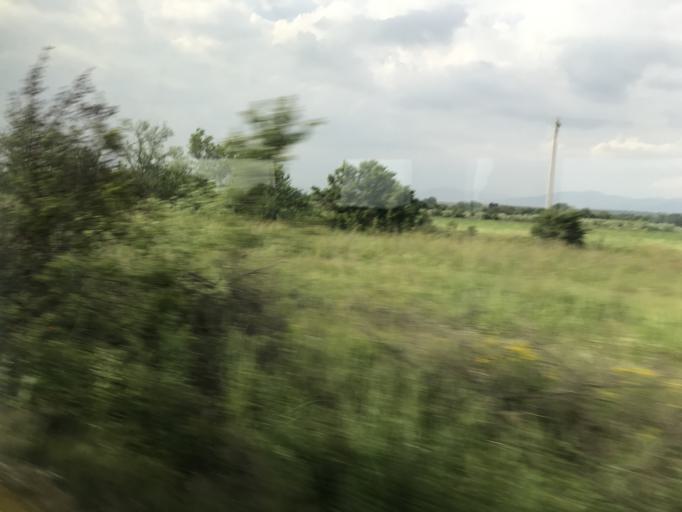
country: GR
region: East Macedonia and Thrace
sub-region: Nomos Rodopis
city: Sapes
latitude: 41.0367
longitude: 25.6696
